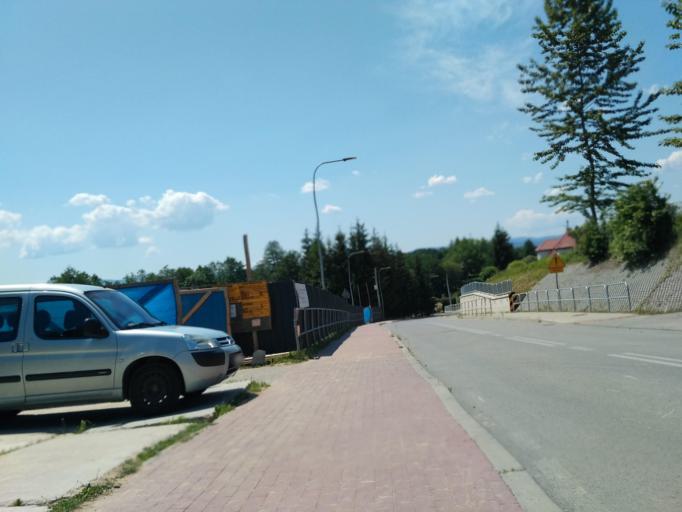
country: PL
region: Subcarpathian Voivodeship
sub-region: Krosno
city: Krosno
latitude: 49.7047
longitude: 21.7796
